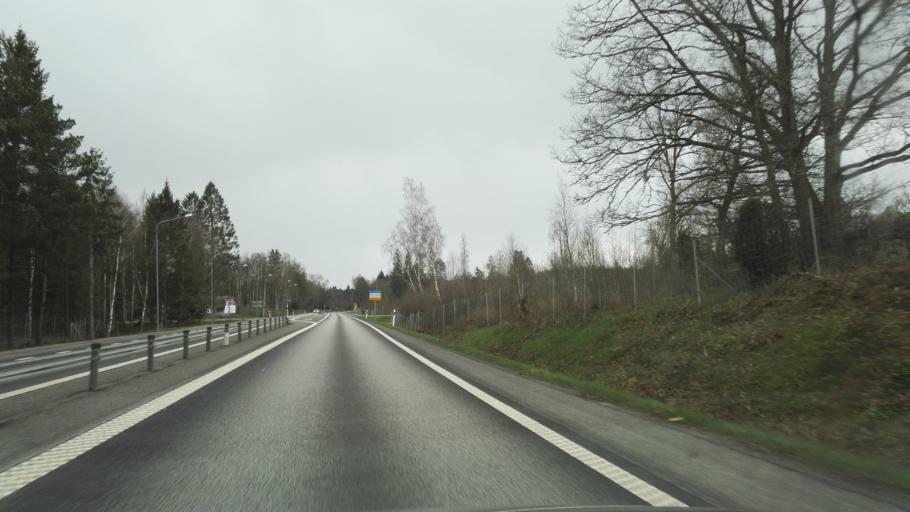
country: SE
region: Skane
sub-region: Osby Kommun
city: Osby
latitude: 56.3067
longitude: 14.0068
